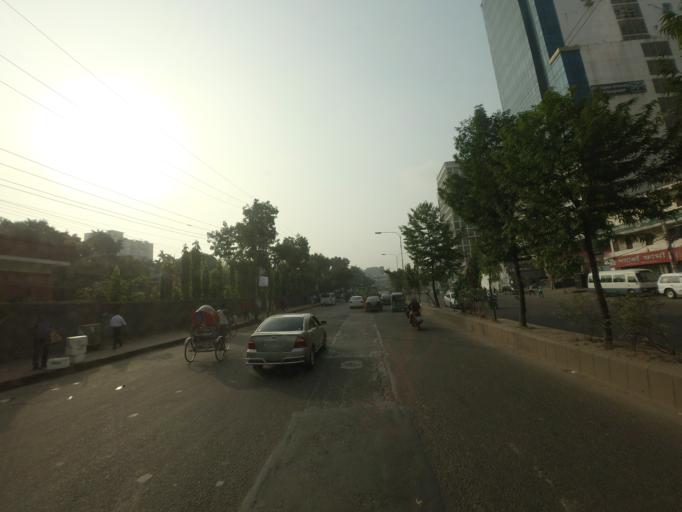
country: BD
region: Dhaka
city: Azimpur
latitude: 23.7745
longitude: 90.3662
